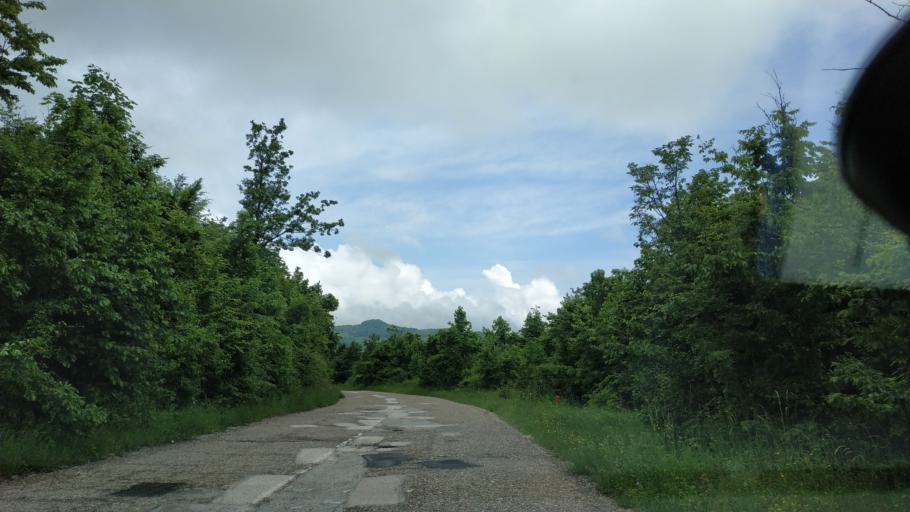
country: RS
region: Central Serbia
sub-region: Zajecarski Okrug
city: Boljevac
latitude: 43.7236
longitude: 21.9527
